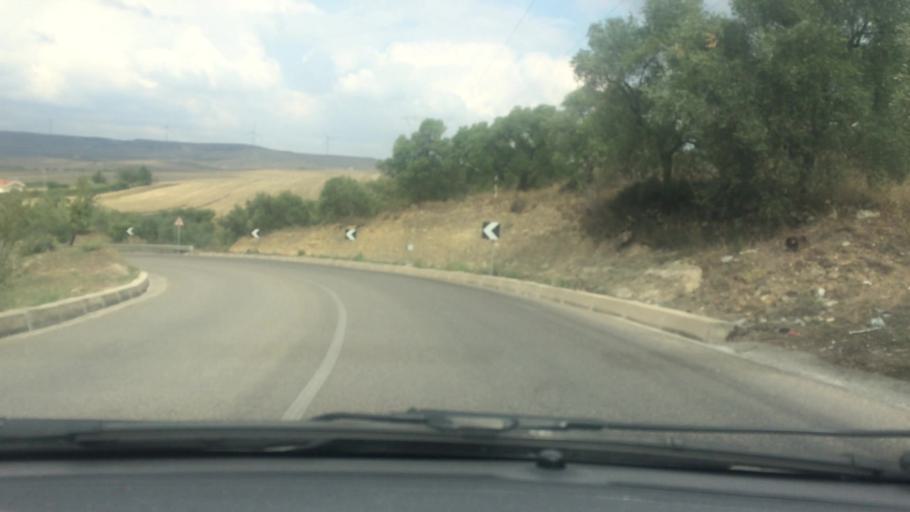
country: IT
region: Basilicate
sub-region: Provincia di Matera
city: Matera
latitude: 40.6884
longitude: 16.5694
